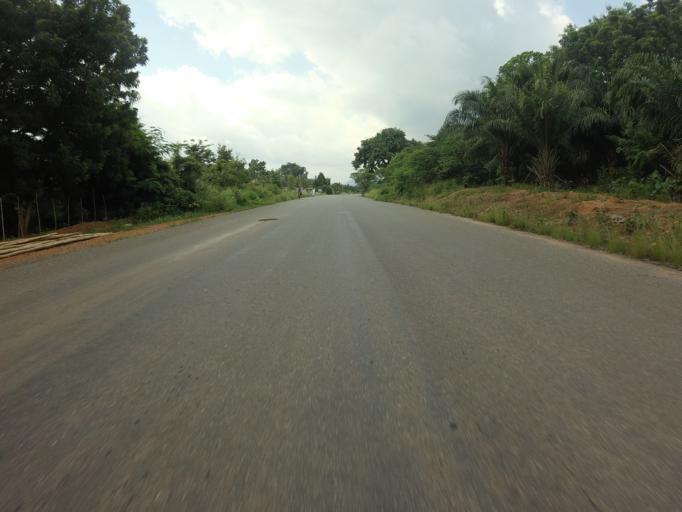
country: GH
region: Volta
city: Kpandu
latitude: 6.8883
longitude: 0.4236
